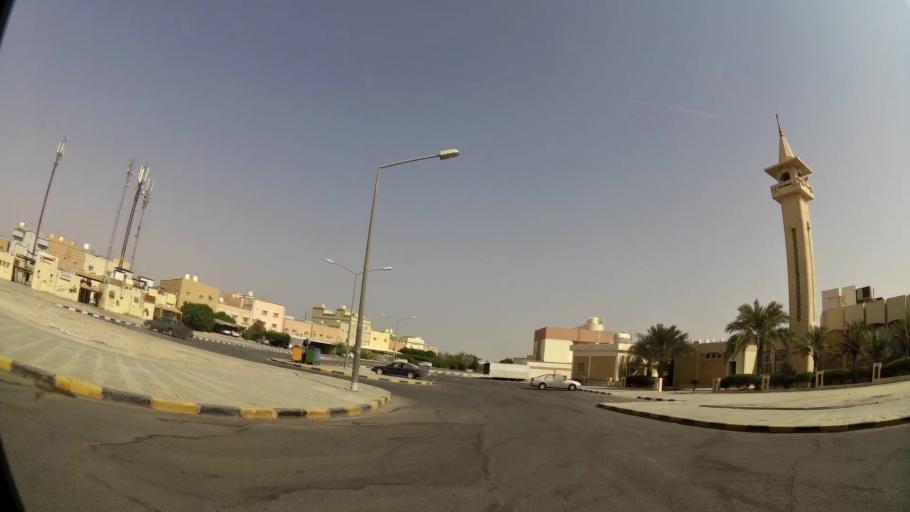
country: KW
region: Muhafazat al Jahra'
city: Al Jahra'
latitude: 29.3267
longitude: 47.6504
